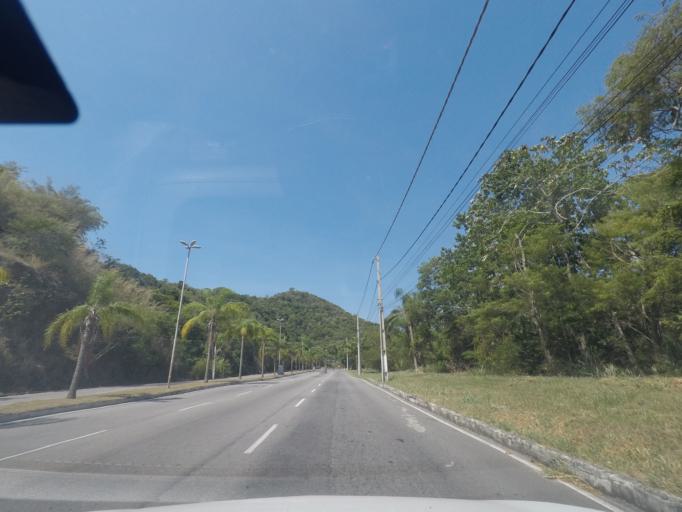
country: BR
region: Rio de Janeiro
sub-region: Niteroi
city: Niteroi
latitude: -22.9259
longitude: -43.0614
